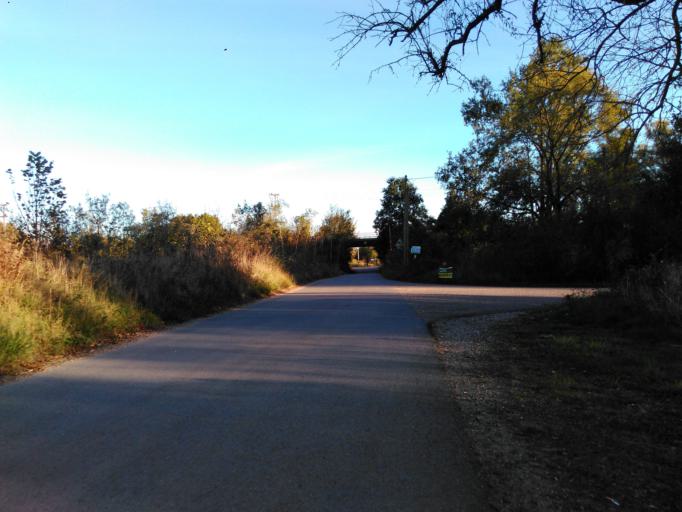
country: FR
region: Lorraine
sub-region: Departement de la Moselle
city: Argancy
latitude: 49.1959
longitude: 6.1859
